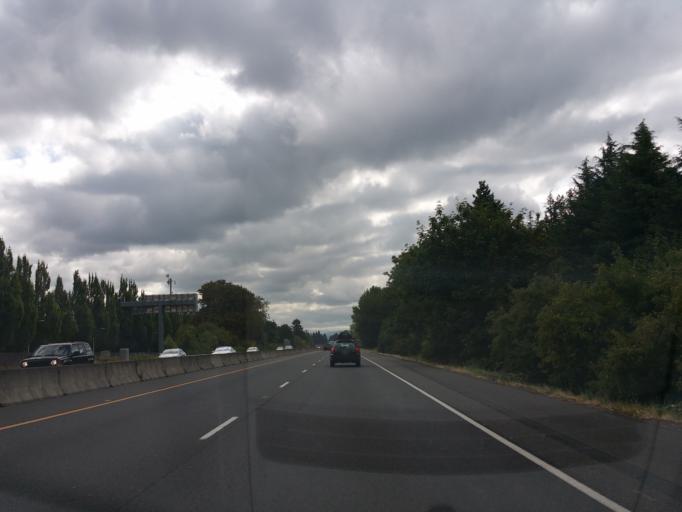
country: US
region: Washington
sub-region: Clark County
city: Mill Plain
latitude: 45.5964
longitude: -122.5209
